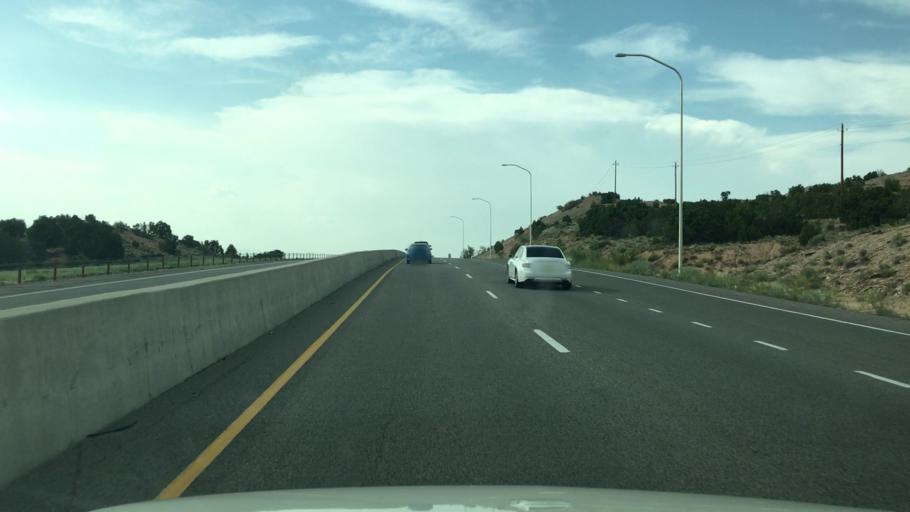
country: US
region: New Mexico
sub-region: Santa Fe County
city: Santa Fe
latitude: 35.7882
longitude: -105.9507
